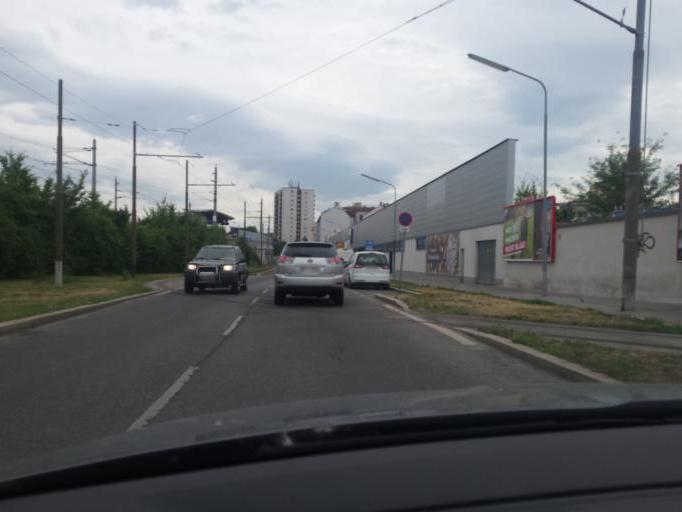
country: AT
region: Vienna
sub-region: Wien Stadt
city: Vienna
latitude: 48.1775
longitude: 16.4077
